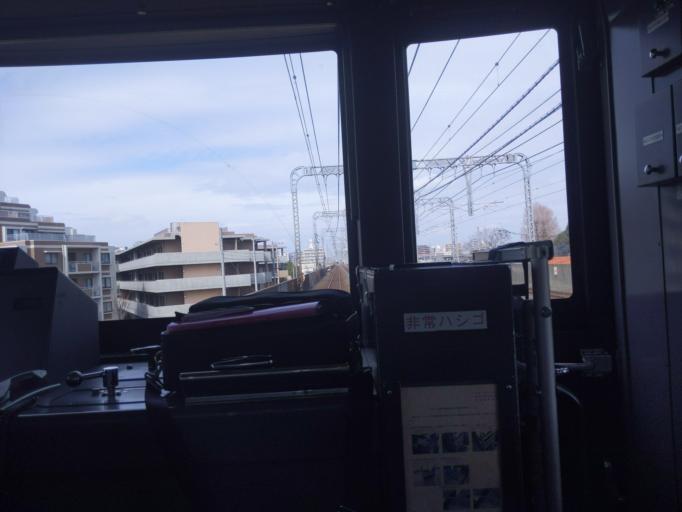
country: JP
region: Saitama
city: Koshigaya
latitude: 35.8584
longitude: 139.7937
